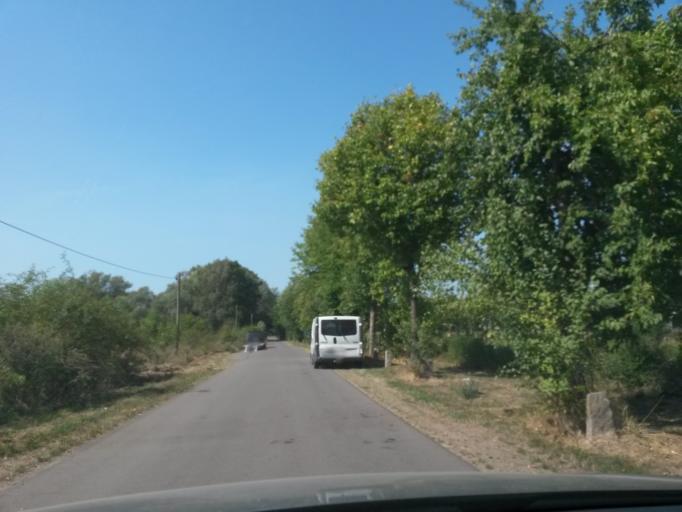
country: DE
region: Saxony-Anhalt
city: Jerichow
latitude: 52.4015
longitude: 11.9832
